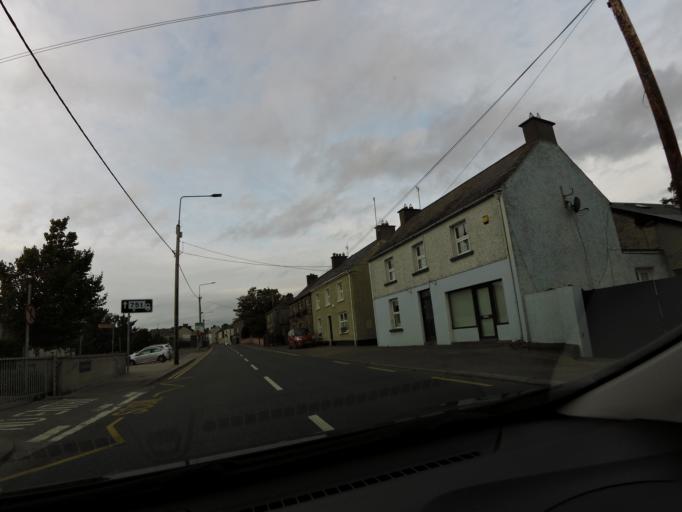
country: IE
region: Leinster
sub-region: Uibh Fhaili
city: Ferbane
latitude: 53.2692
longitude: -7.8280
